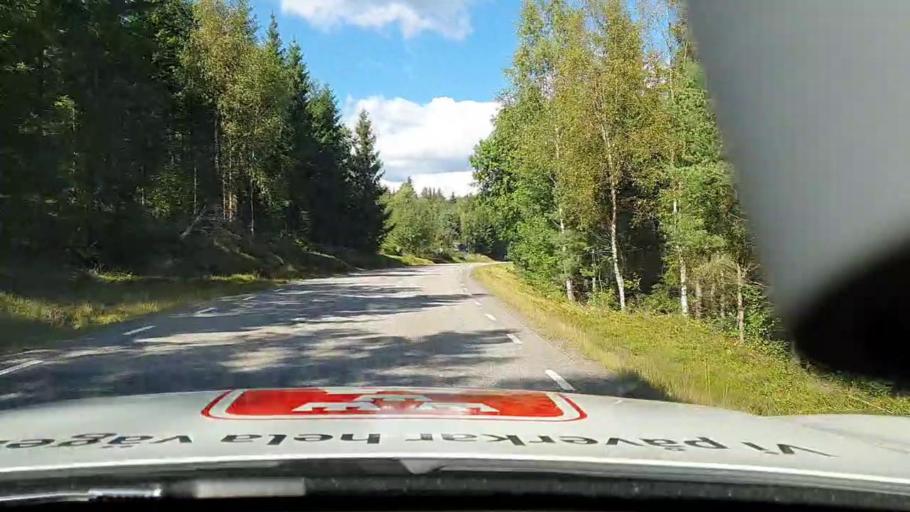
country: SE
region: Vaestra Goetaland
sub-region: Marks Kommun
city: Fritsla
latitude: 57.3703
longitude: 12.8618
